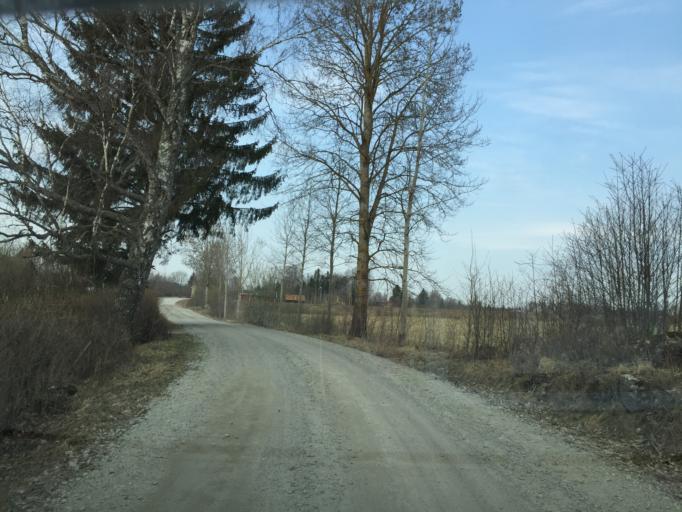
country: SE
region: Soedermanland
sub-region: Vingakers Kommun
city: Vingaker
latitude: 59.0445
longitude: 15.7877
